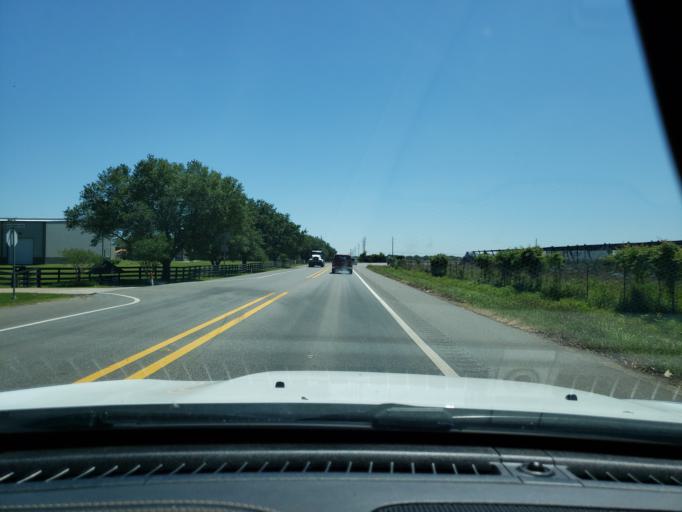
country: US
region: Texas
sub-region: Fort Bend County
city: Fulshear
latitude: 29.6853
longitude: -95.8419
